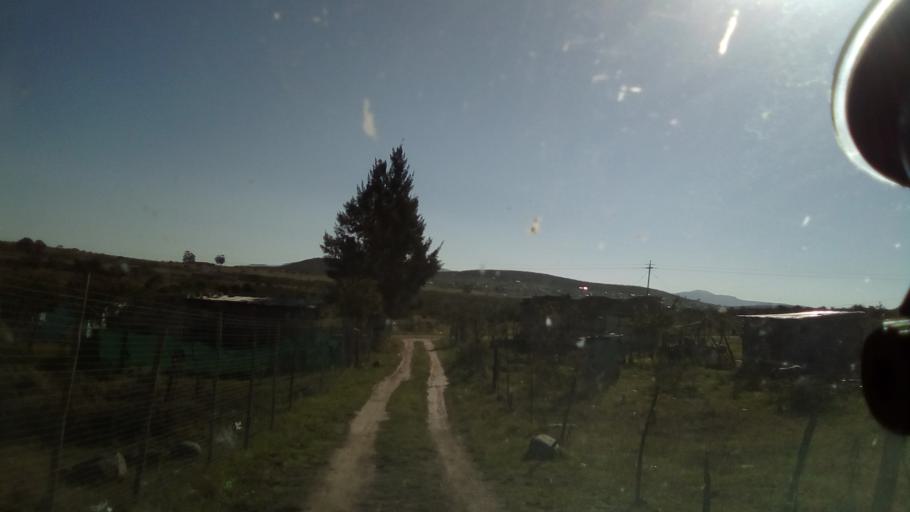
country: ZA
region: Eastern Cape
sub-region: Buffalo City Metropolitan Municipality
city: Bhisho
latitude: -32.8259
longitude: 27.3684
